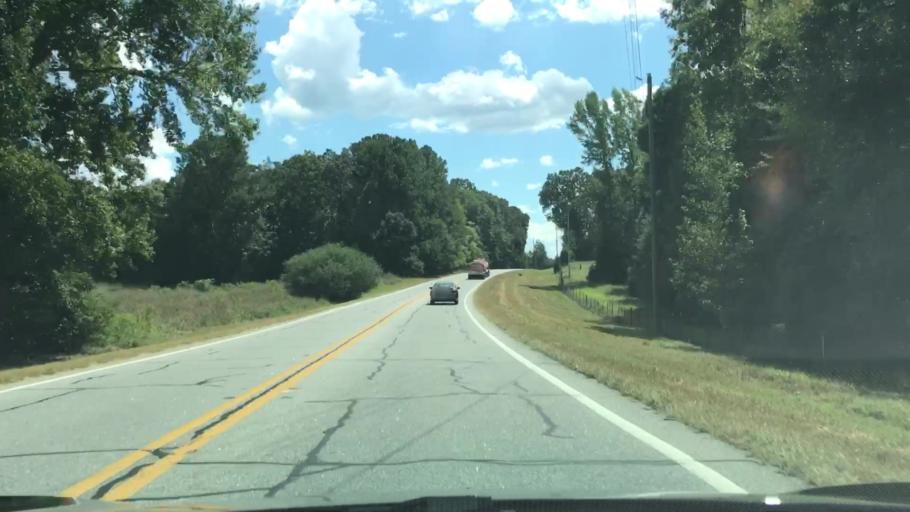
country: US
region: Georgia
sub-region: Oconee County
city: Watkinsville
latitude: 33.7507
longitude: -83.3016
